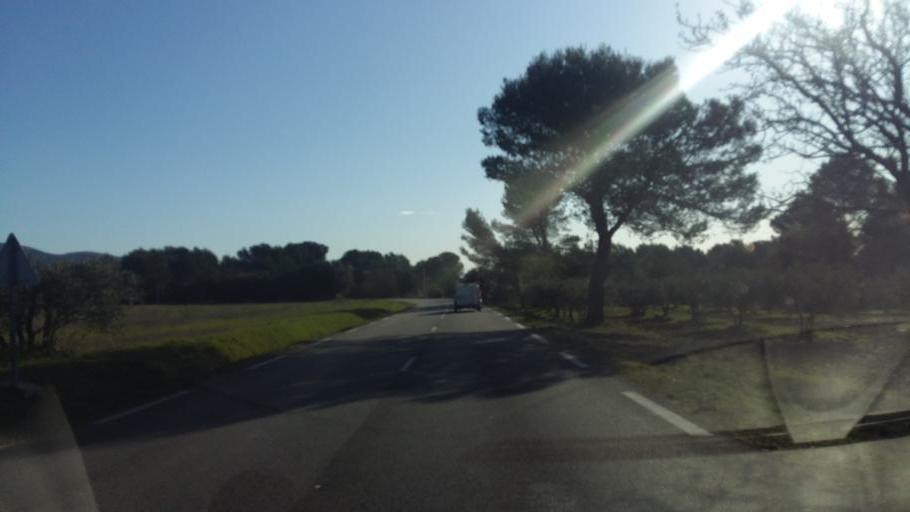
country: FR
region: Provence-Alpes-Cote d'Azur
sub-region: Departement des Bouches-du-Rhone
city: Charleval
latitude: 43.7496
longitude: 5.2576
